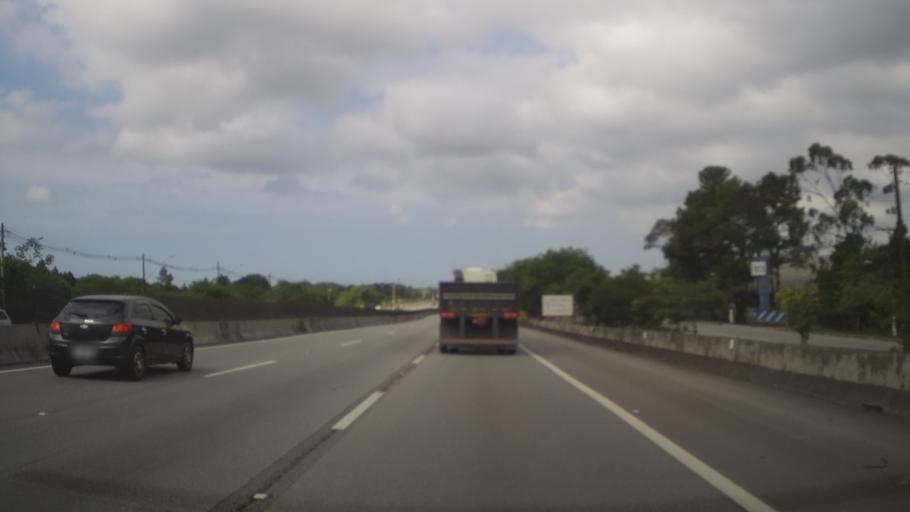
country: BR
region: Sao Paulo
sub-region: Cubatao
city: Cubatao
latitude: -23.9562
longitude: -46.4680
